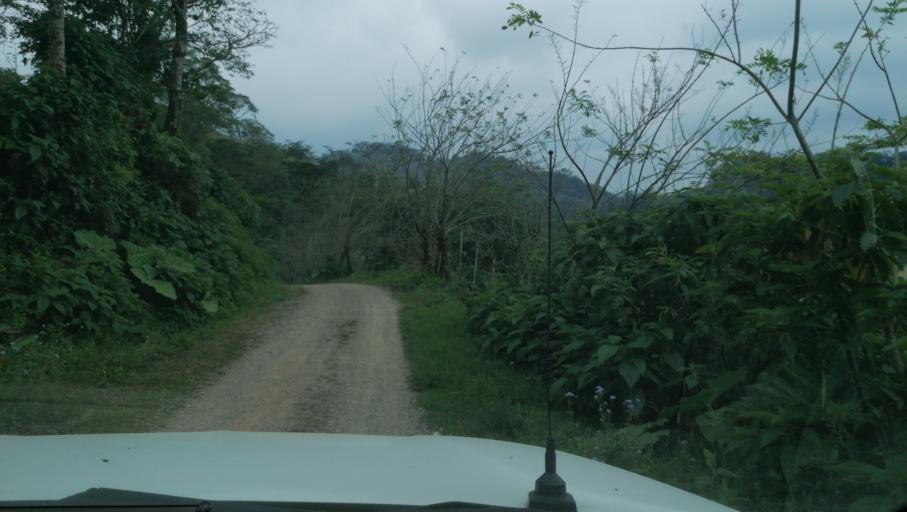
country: MX
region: Chiapas
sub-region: Francisco Leon
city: San Miguel la Sardina
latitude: 17.3369
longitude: -93.3135
